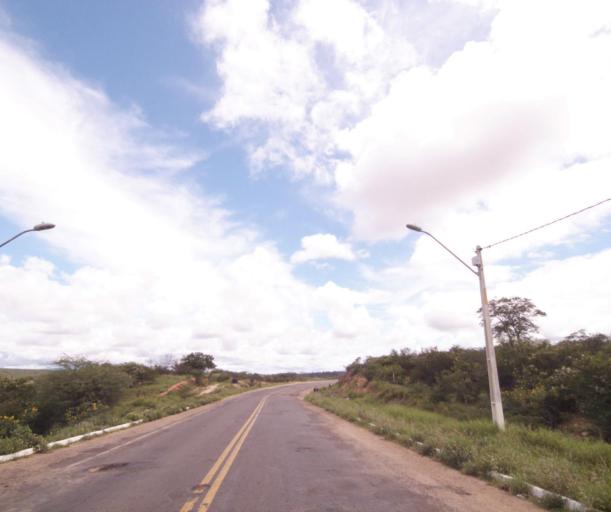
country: BR
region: Bahia
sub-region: Tanhacu
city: Tanhacu
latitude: -14.1570
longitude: -41.2042
